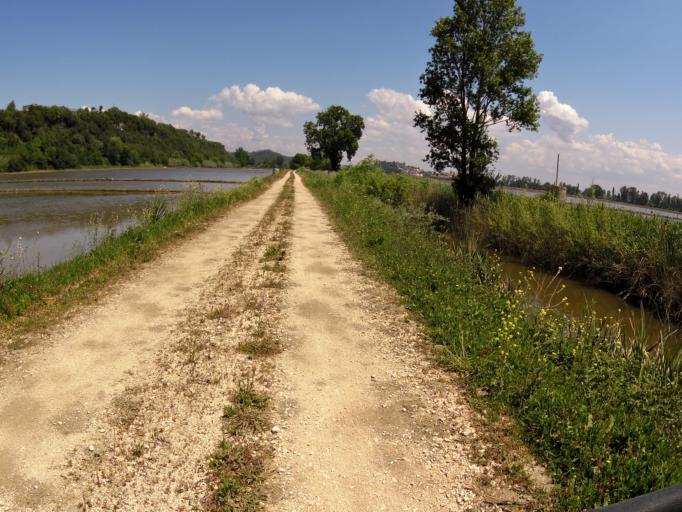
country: PT
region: Coimbra
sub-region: Montemor-O-Velho
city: Montemor-o-Velho
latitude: 40.1694
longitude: -8.7075
